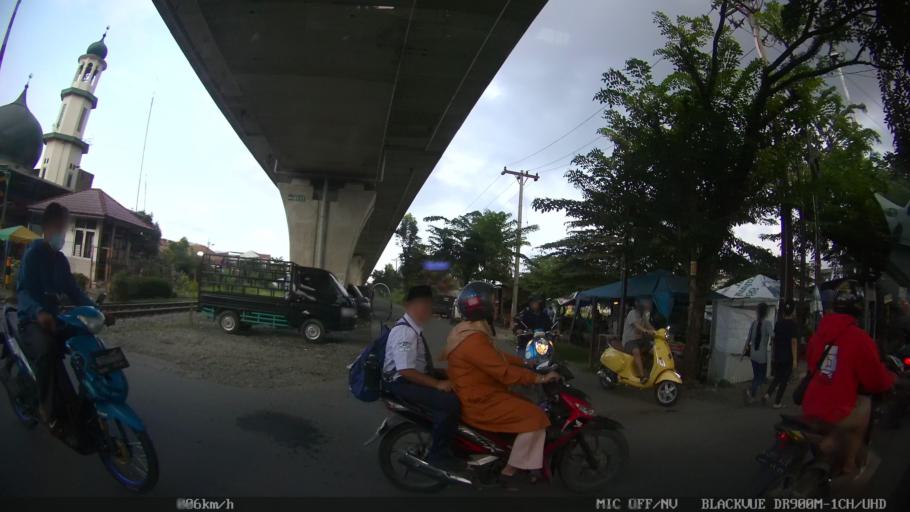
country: ID
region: North Sumatra
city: Medan
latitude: 3.5892
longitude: 98.7115
